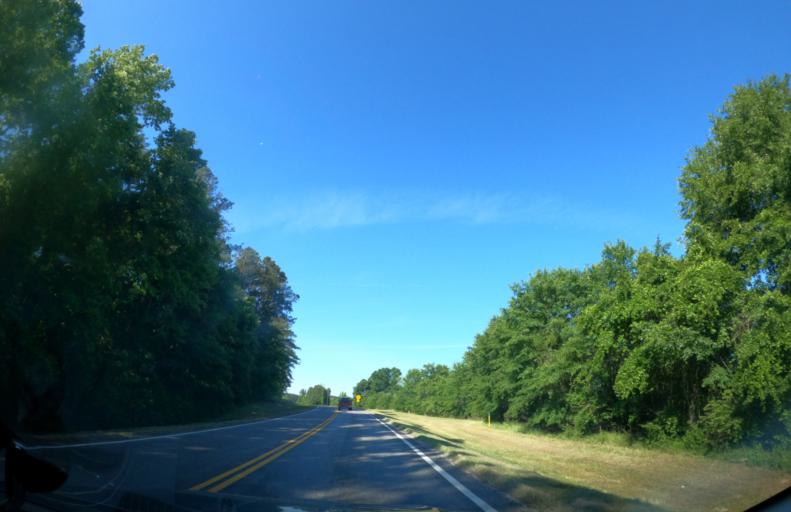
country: US
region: Georgia
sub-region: Columbia County
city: Harlem
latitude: 33.3474
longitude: -82.3484
